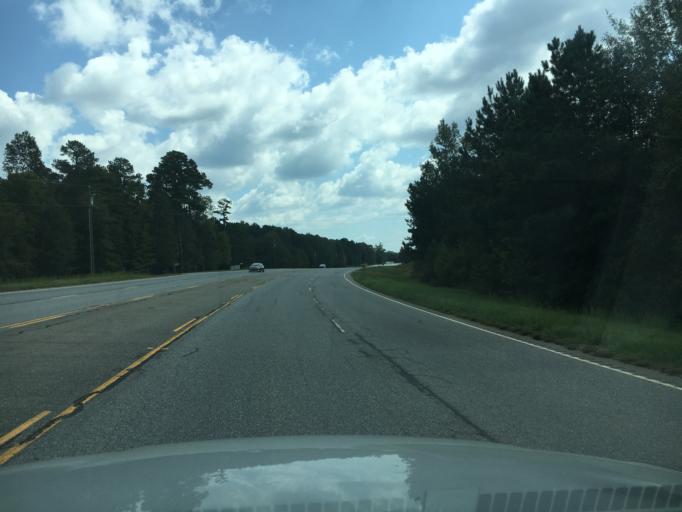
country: US
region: South Carolina
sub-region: Greenwood County
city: Ware Shoals
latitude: 34.4664
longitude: -82.2581
